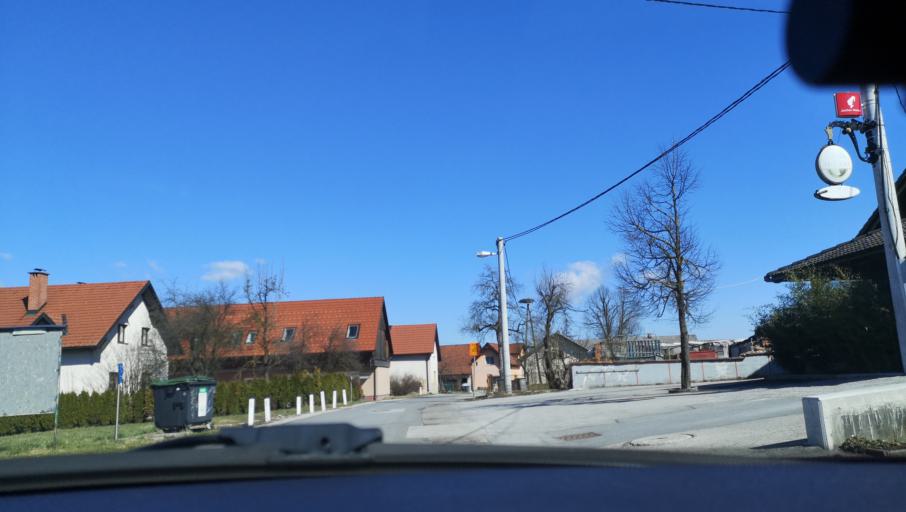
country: SI
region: Ig
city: Ig
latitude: 45.9579
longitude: 14.5144
